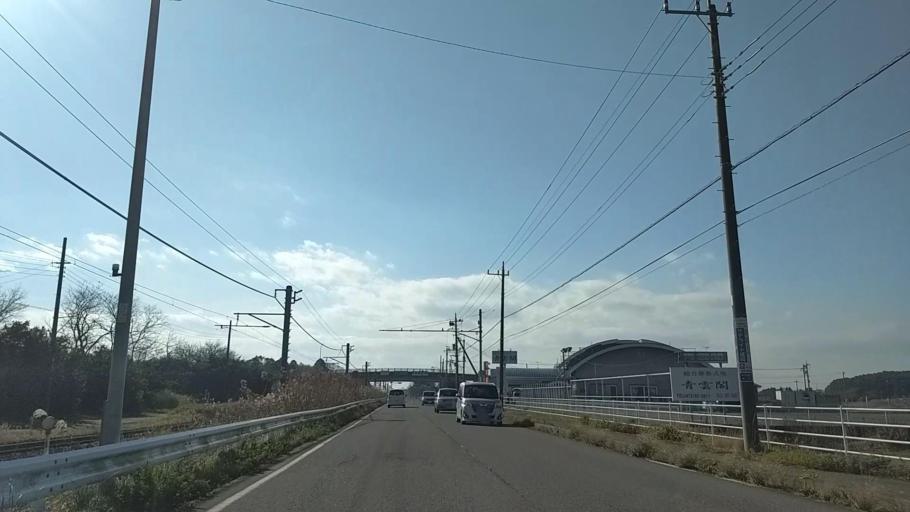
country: JP
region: Chiba
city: Yokaichiba
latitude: 35.6773
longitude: 140.5117
